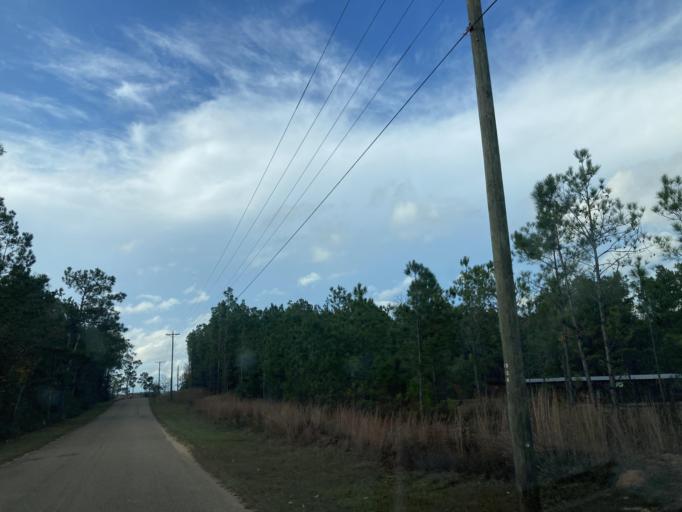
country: US
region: Mississippi
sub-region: Lamar County
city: Purvis
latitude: 31.1398
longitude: -89.6234
